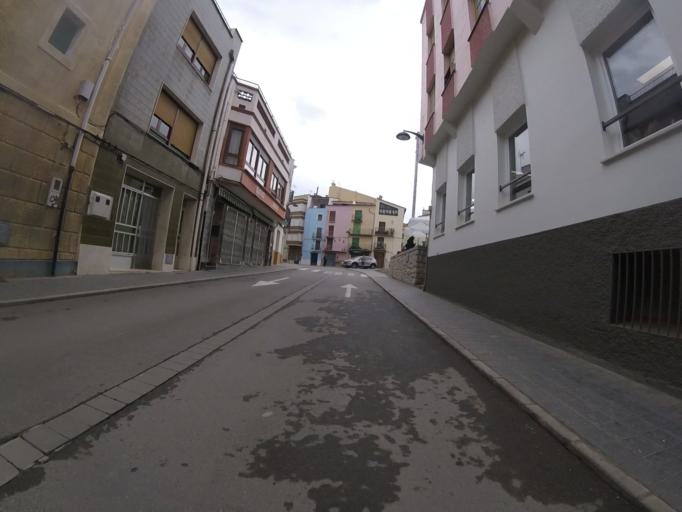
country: ES
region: Valencia
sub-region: Provincia de Castello
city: Cuevas de Vinroma
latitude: 40.3097
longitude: 0.1217
